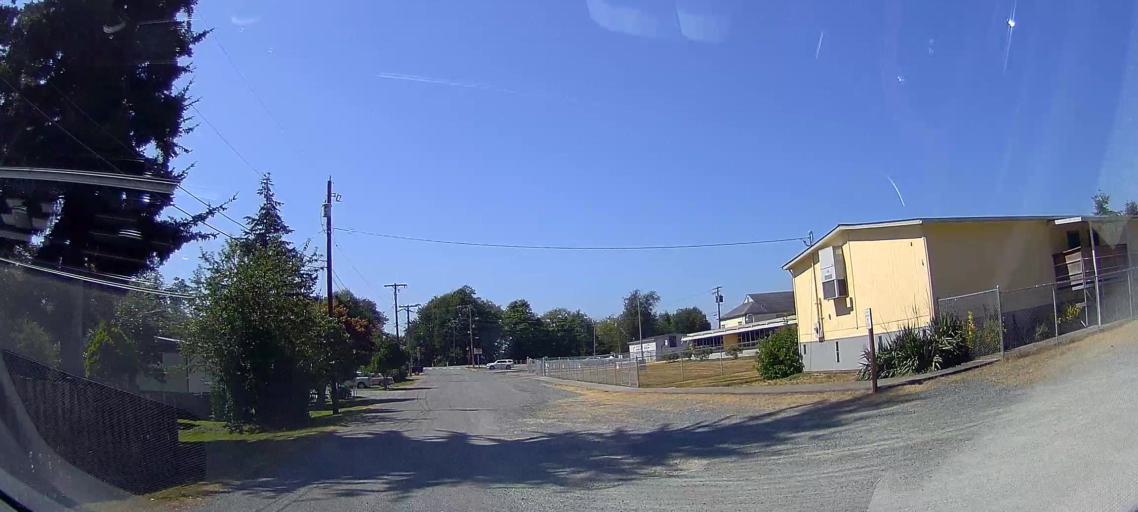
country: US
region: Washington
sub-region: Skagit County
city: Clear Lake
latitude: 48.4643
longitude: -122.2325
